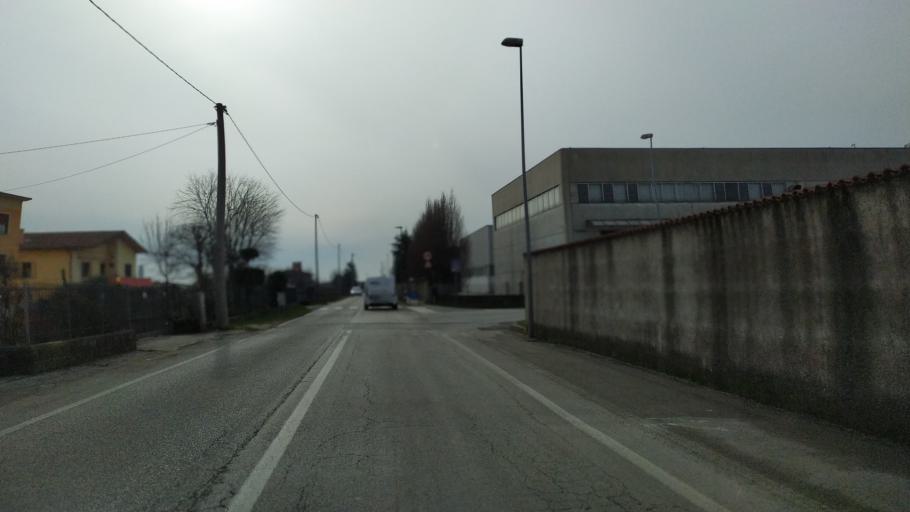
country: IT
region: Veneto
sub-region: Provincia di Vicenza
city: Villaverla
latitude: 45.6500
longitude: 11.5004
